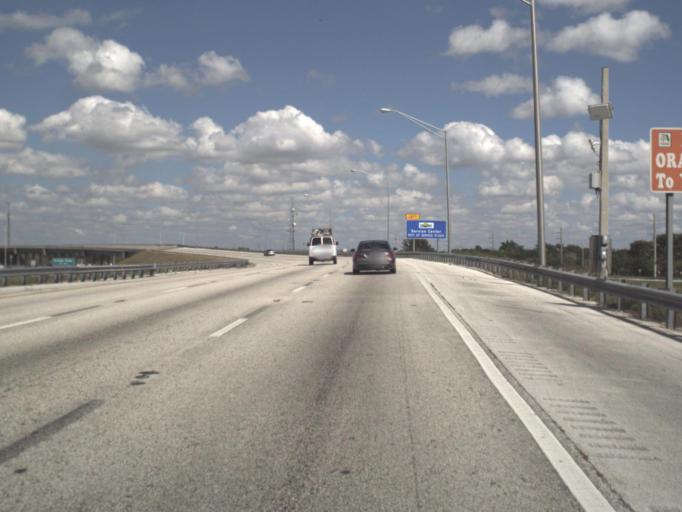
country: US
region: Florida
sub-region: Miami-Dade County
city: Three Lakes
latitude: 25.6467
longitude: -80.3848
